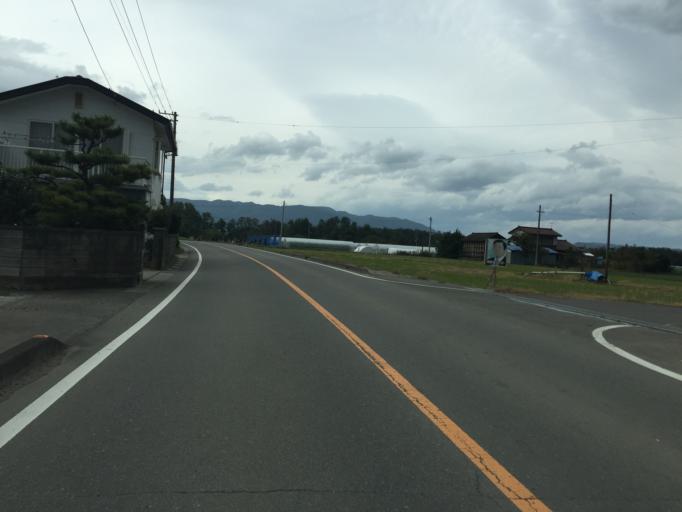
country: JP
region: Fukushima
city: Hobaramachi
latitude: 37.8371
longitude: 140.5590
